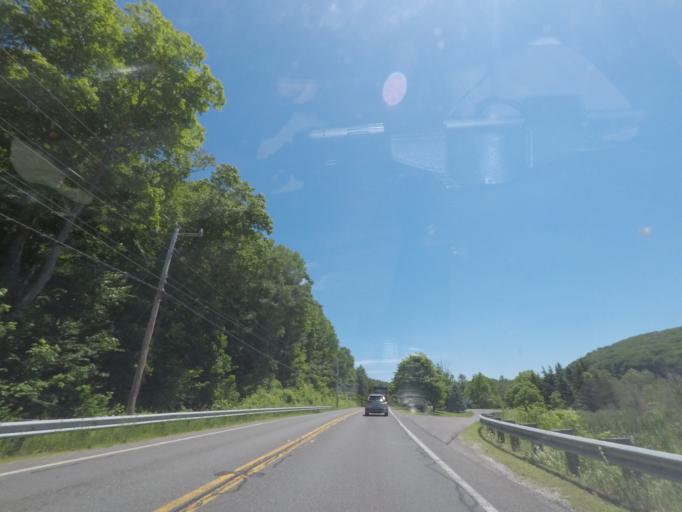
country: US
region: Massachusetts
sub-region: Berkshire County
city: Lee
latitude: 42.2936
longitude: -73.1626
